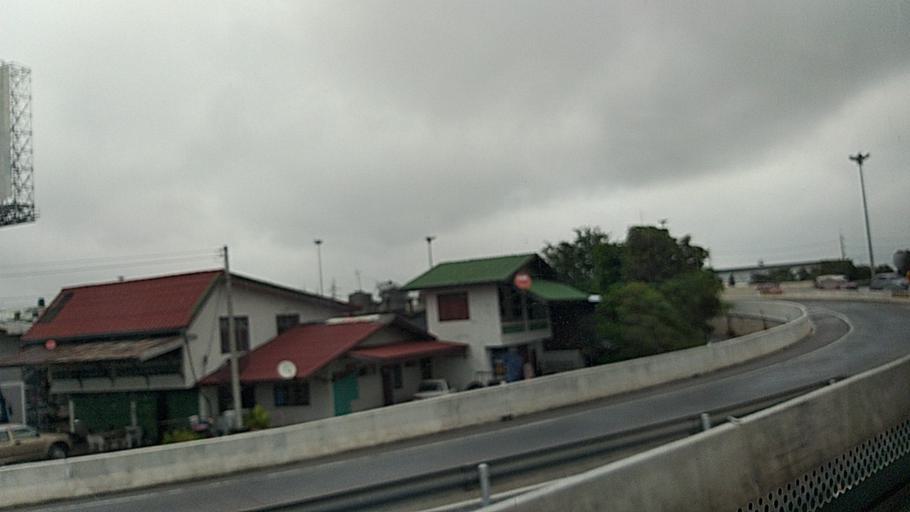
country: TH
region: Nakhon Ratchasima
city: Nakhon Ratchasima
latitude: 14.9579
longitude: 102.0517
